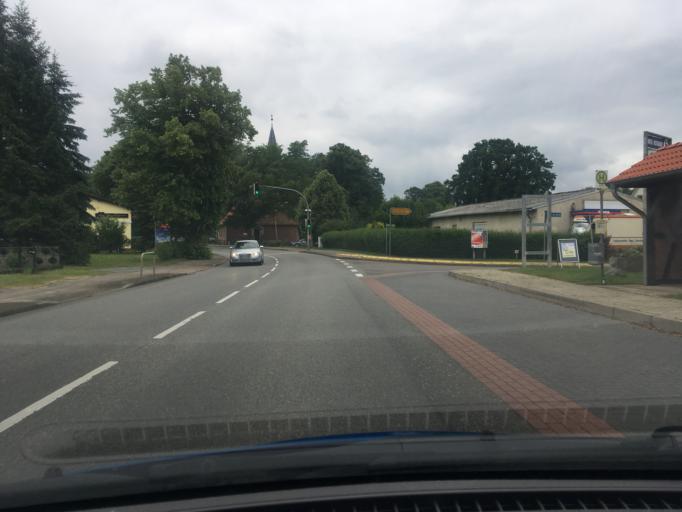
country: DE
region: Mecklenburg-Vorpommern
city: Stralendorf
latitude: 53.5318
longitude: 11.3022
